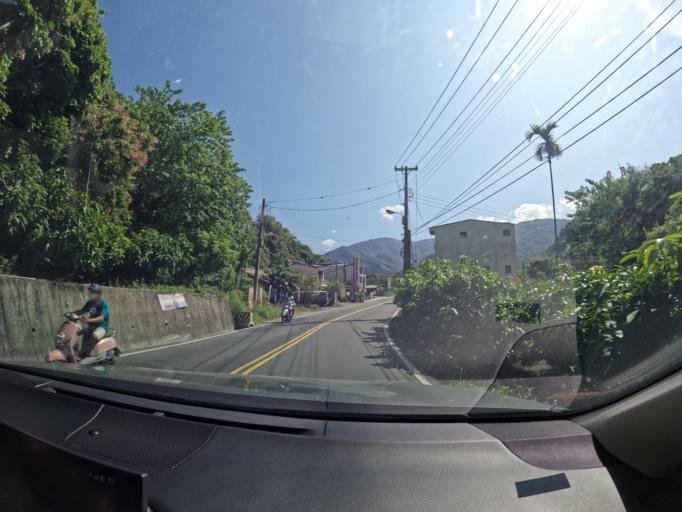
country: TW
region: Taiwan
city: Yujing
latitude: 23.1053
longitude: 120.6930
